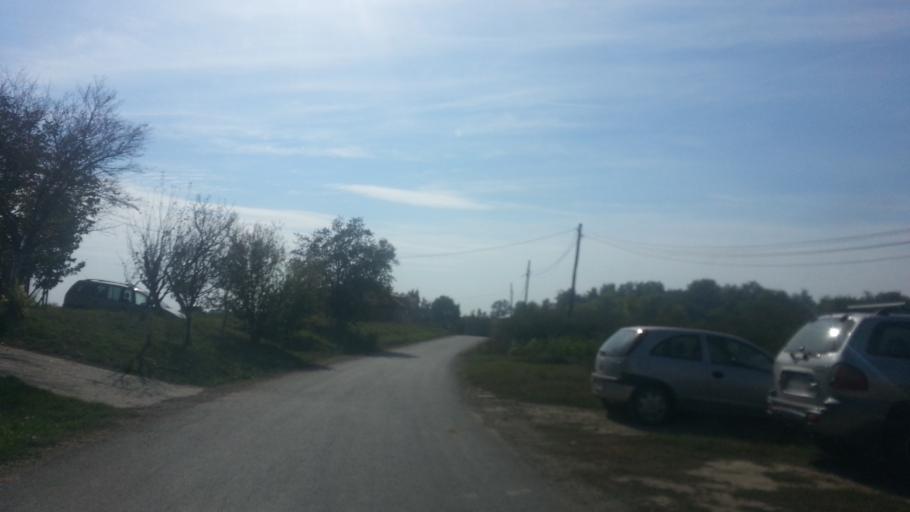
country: RS
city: Stari Banovci
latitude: 44.9962
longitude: 20.2793
